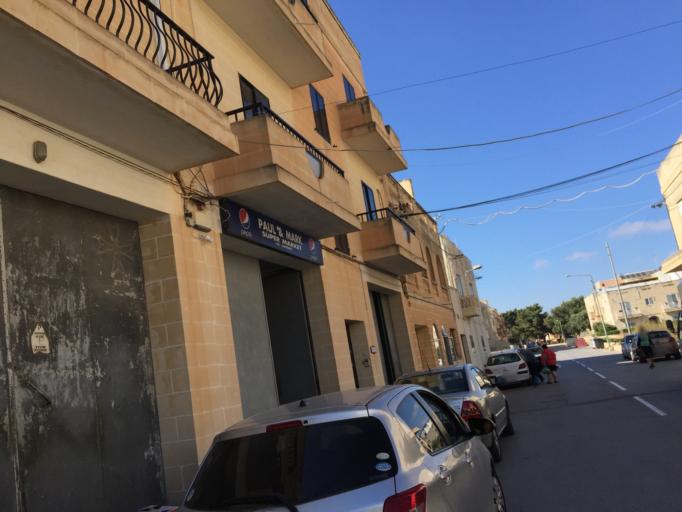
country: MT
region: Il-Qrendi
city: Qrendi
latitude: 35.8361
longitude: 14.4612
